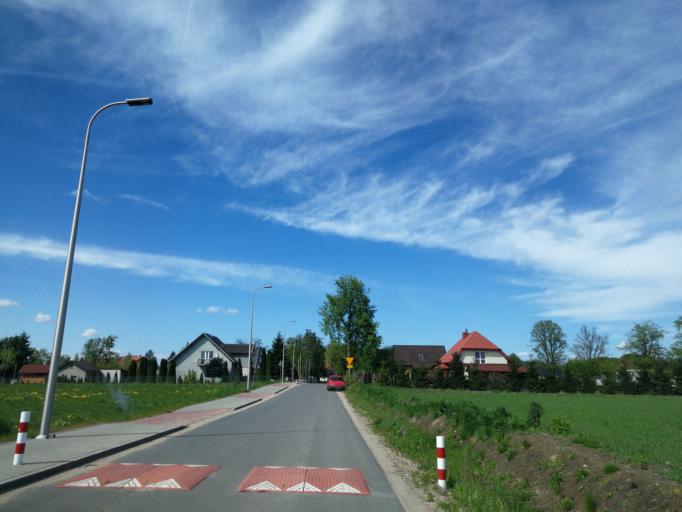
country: PL
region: Warmian-Masurian Voivodeship
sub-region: Powiat ilawski
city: Ilawa
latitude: 53.6276
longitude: 19.6656
